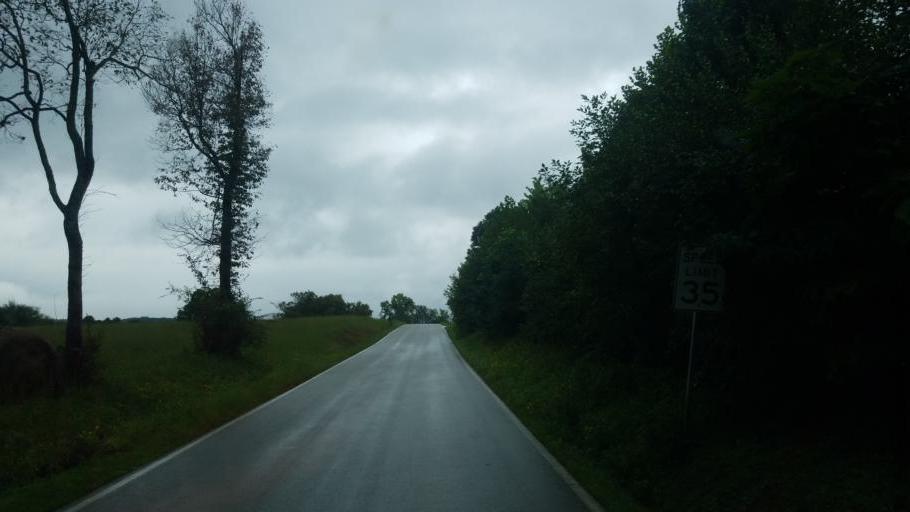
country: US
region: Kentucky
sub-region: Rowan County
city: Morehead
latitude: 38.1613
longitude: -83.5045
